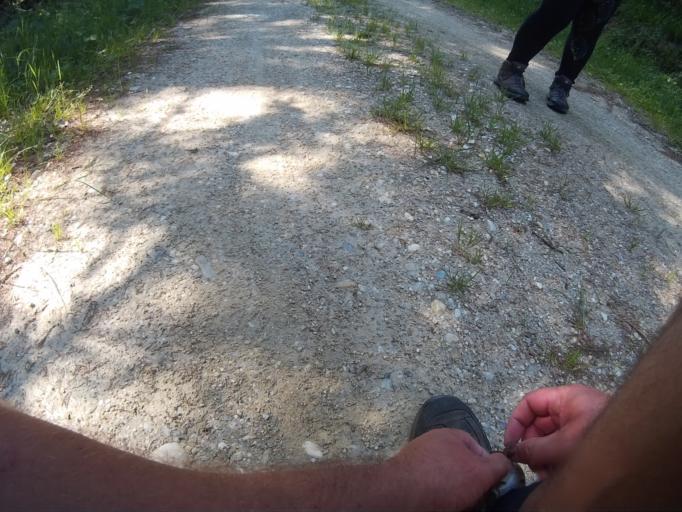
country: AT
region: Burgenland
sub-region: Politischer Bezirk Gussing
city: Heiligenbrunn
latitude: 46.9164
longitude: 16.4677
